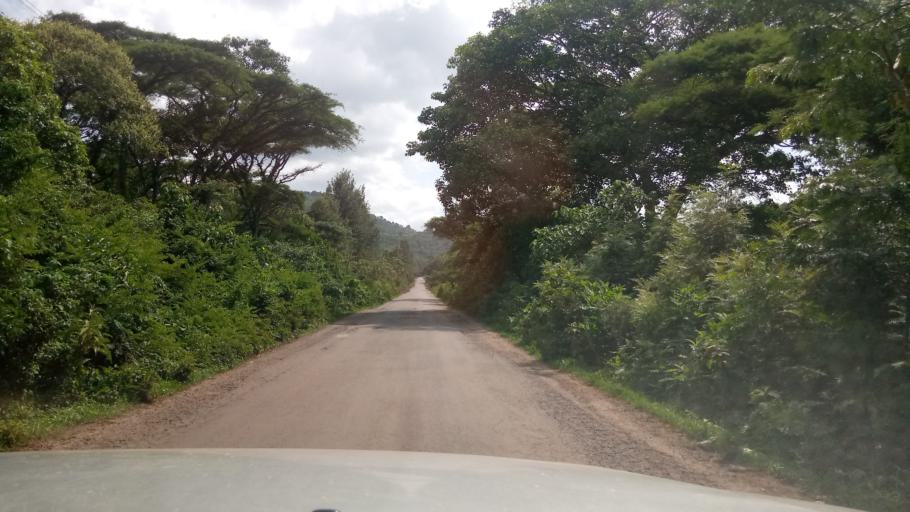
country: ET
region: Oromiya
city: Agaro
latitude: 7.9221
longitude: 36.5293
